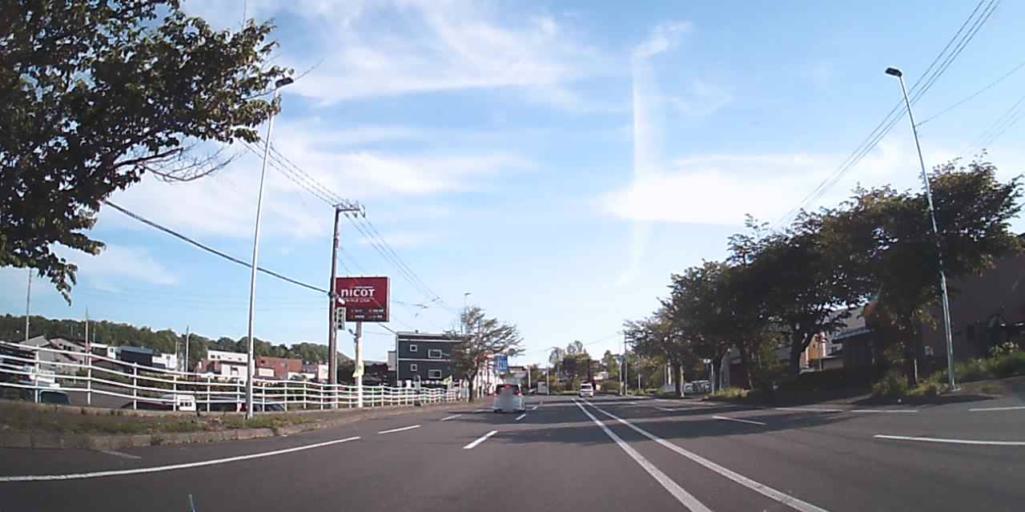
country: JP
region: Hokkaido
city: Shiraoi
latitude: 42.4567
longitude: 141.1772
